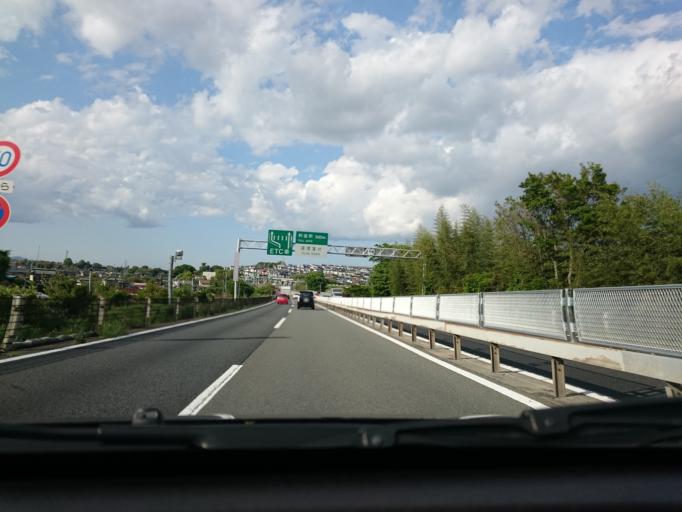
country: JP
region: Kanagawa
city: Oiso
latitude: 35.3328
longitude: 139.2930
